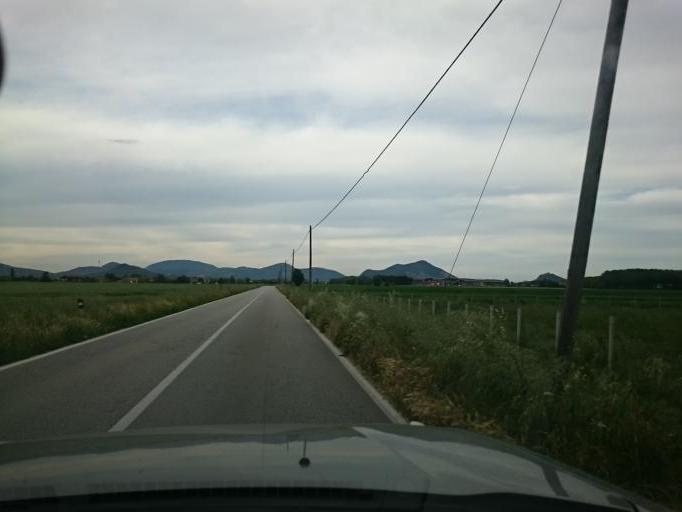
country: IT
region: Veneto
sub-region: Provincia di Padova
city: Sant'Elena
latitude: 45.1947
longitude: 11.7166
